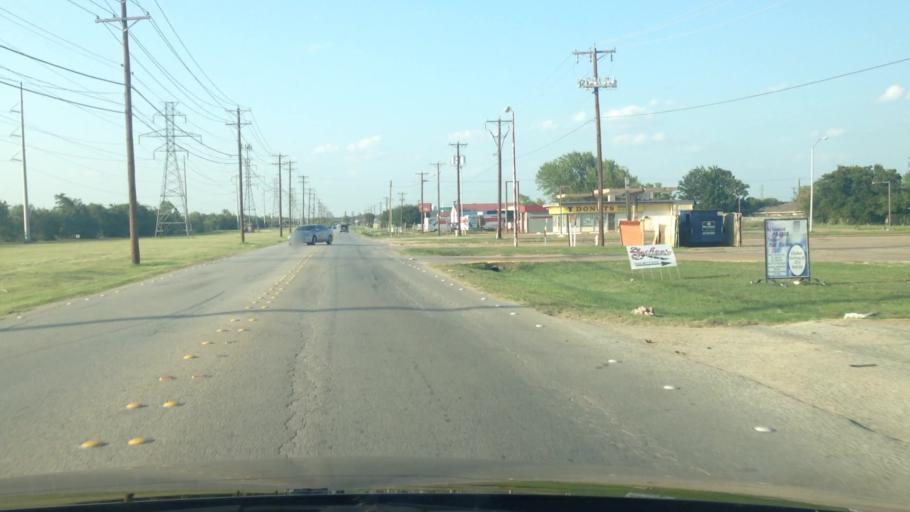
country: US
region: Texas
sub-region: Tarrant County
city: Everman
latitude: 32.6469
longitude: -97.2852
